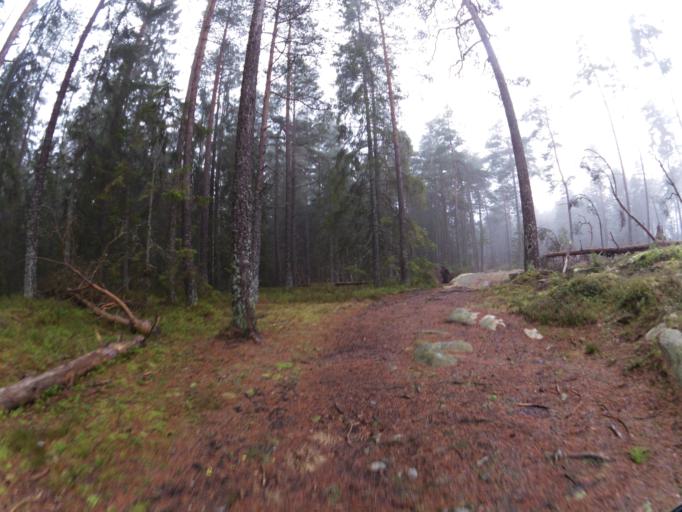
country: NO
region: Ostfold
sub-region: Fredrikstad
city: Fredrikstad
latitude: 59.2625
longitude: 10.9842
